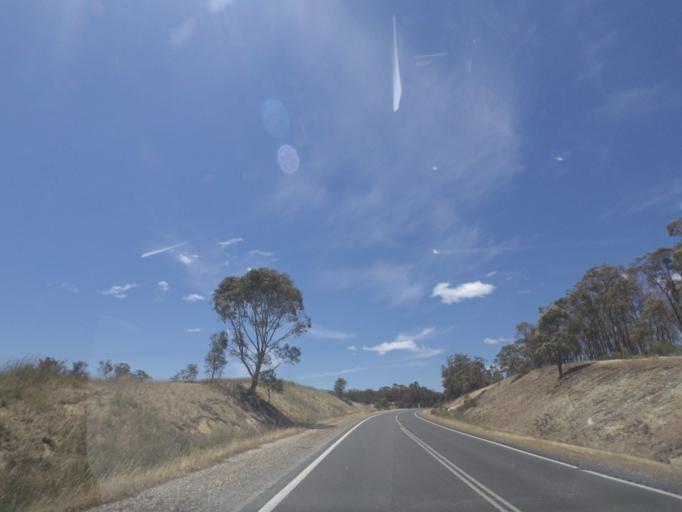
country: AU
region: Victoria
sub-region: Mount Alexander
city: Castlemaine
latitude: -37.1667
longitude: 144.1481
